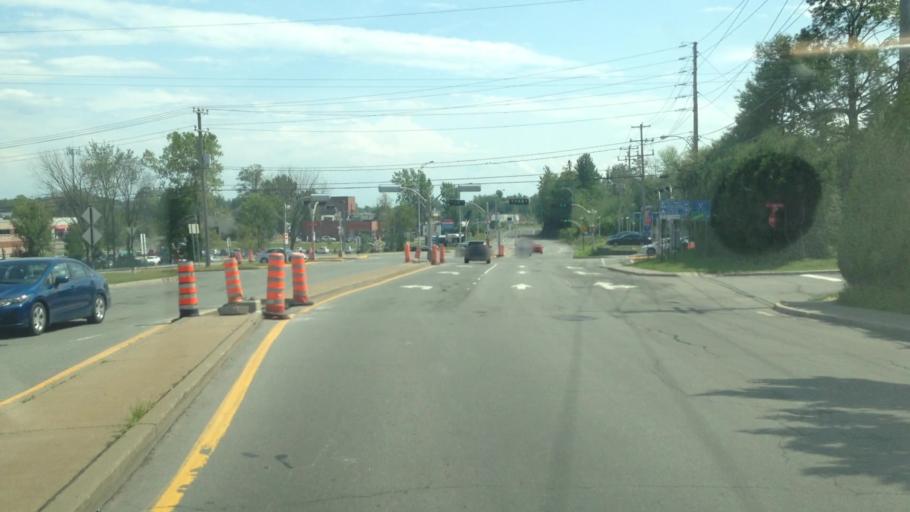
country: CA
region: Quebec
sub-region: Laurentides
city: Saint-Jerome
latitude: 45.7967
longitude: -74.0295
